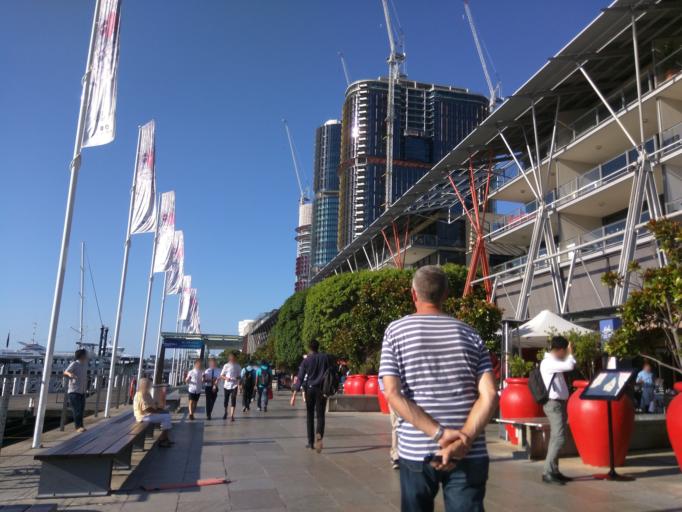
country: AU
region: New South Wales
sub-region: City of Sydney
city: Sydney
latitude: -33.8679
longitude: 151.2014
